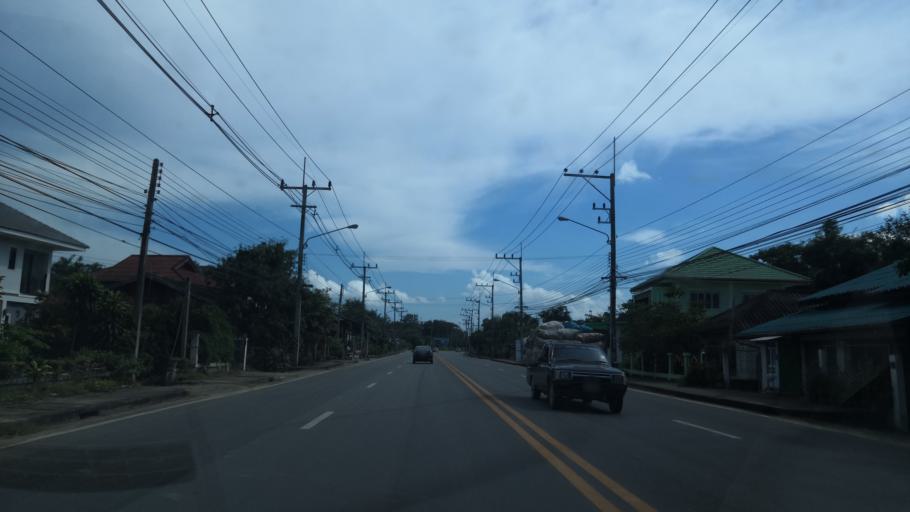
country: TH
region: Chiang Rai
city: Wiang Pa Pao
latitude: 19.2563
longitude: 99.5123
